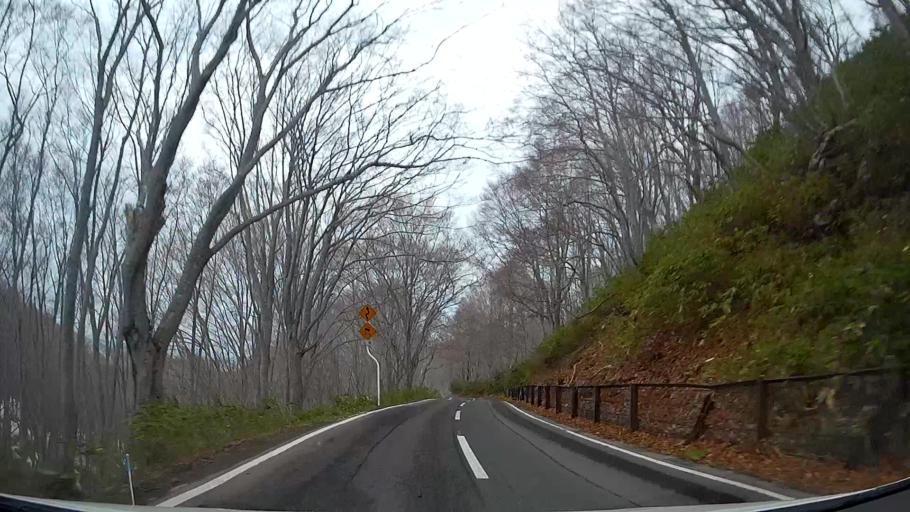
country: JP
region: Aomori
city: Aomori Shi
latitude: 40.6498
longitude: 140.8464
